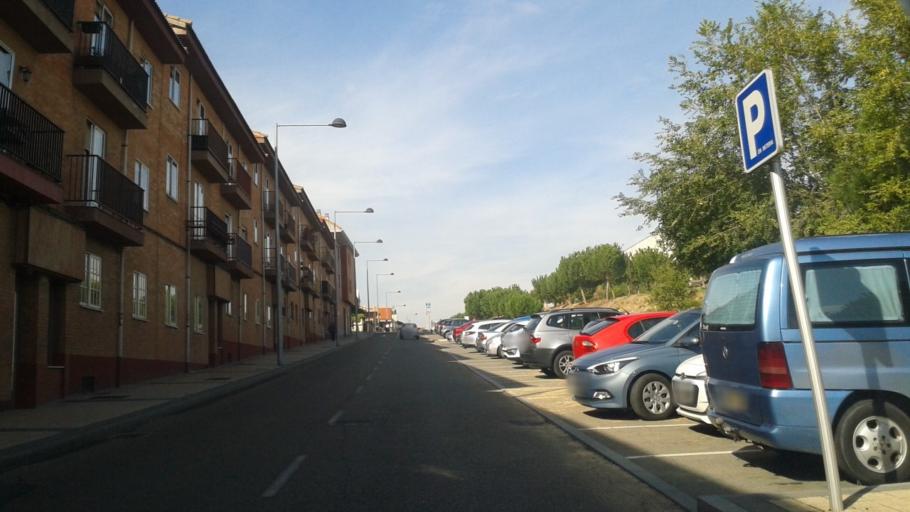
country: ES
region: Castille and Leon
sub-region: Provincia de Valladolid
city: Arroyo
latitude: 41.6263
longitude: -4.7677
